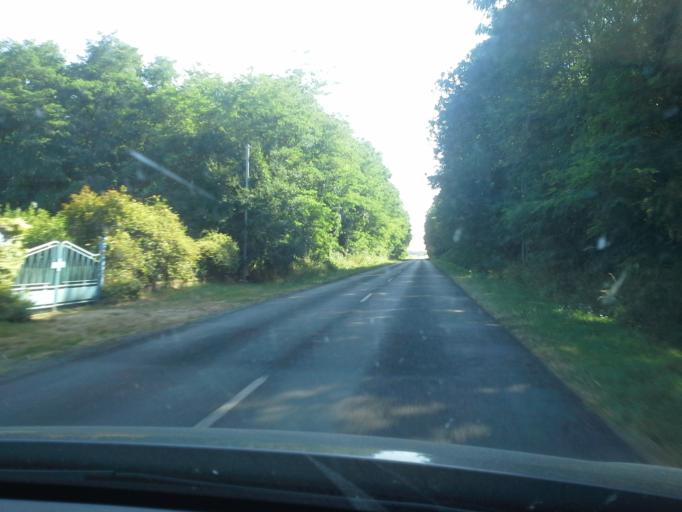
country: FR
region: Centre
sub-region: Departement du Loir-et-Cher
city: Cande-sur-Beuvron
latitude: 47.4999
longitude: 1.2690
